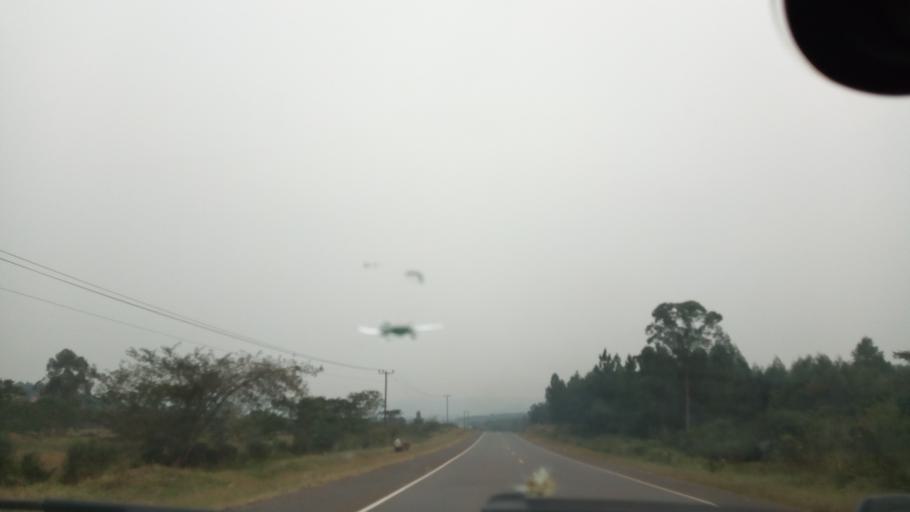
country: UG
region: Western Region
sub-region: Mbarara District
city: Mbarara
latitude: -0.7199
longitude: 30.7264
